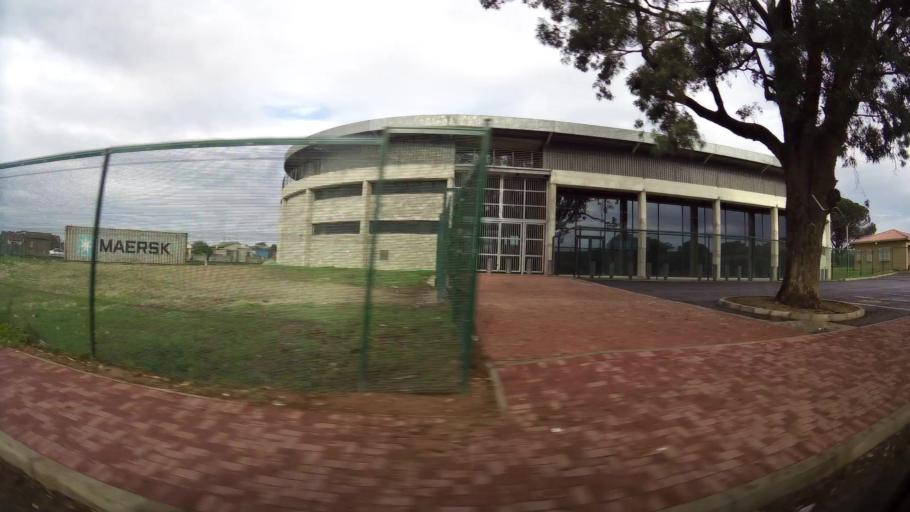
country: ZA
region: Eastern Cape
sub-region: Nelson Mandela Bay Metropolitan Municipality
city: Port Elizabeth
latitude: -33.9852
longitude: 25.5869
